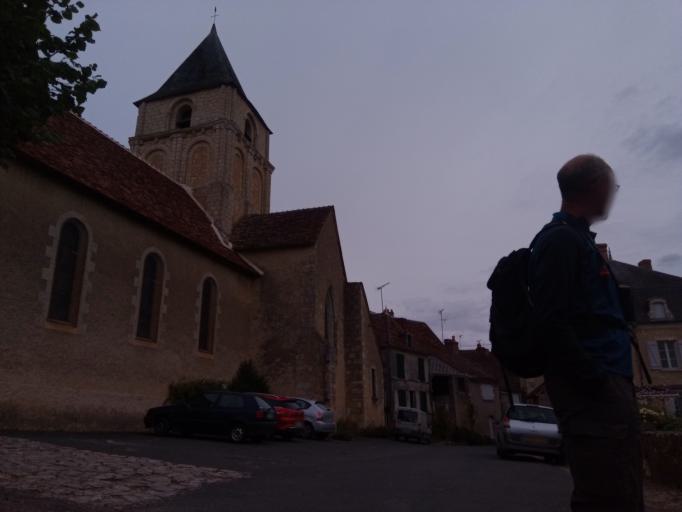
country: FR
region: Centre
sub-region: Departement de l'Indre
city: Tournon-Saint-Martin
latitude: 46.6956
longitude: 0.8833
